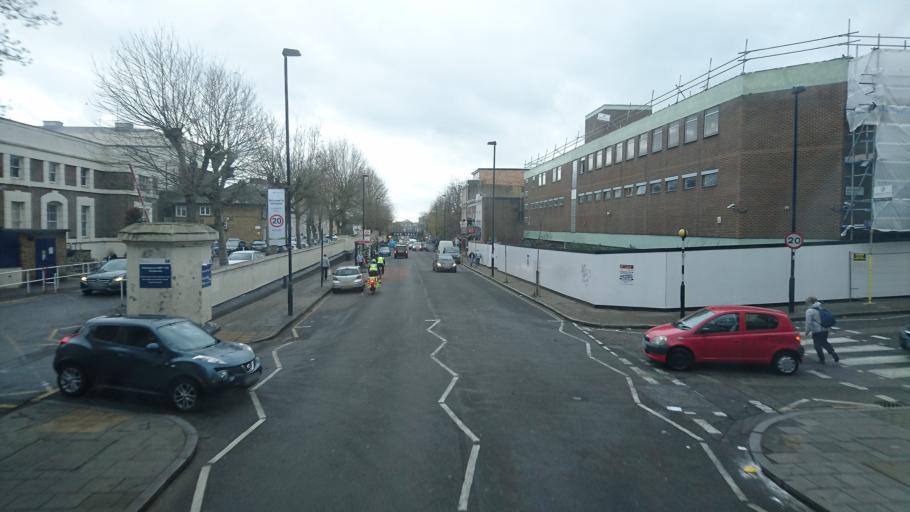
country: GB
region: England
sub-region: Greater London
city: Barnsbury
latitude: 51.5458
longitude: -0.1179
